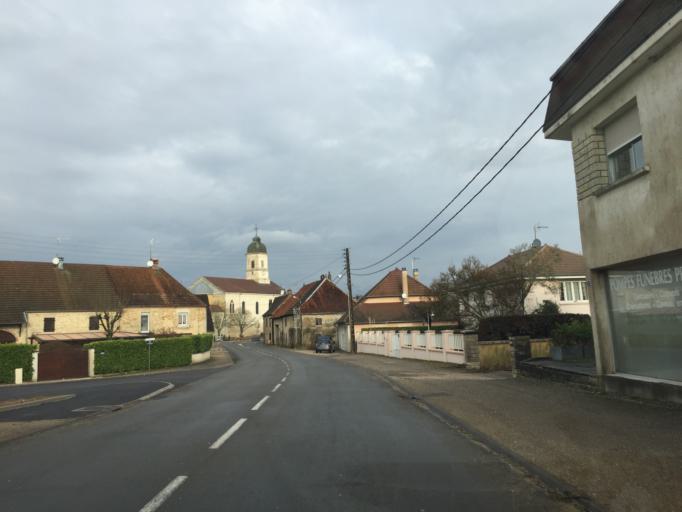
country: FR
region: Franche-Comte
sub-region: Departement du Jura
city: Mont-sous-Vaudrey
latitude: 46.9773
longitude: 5.6034
